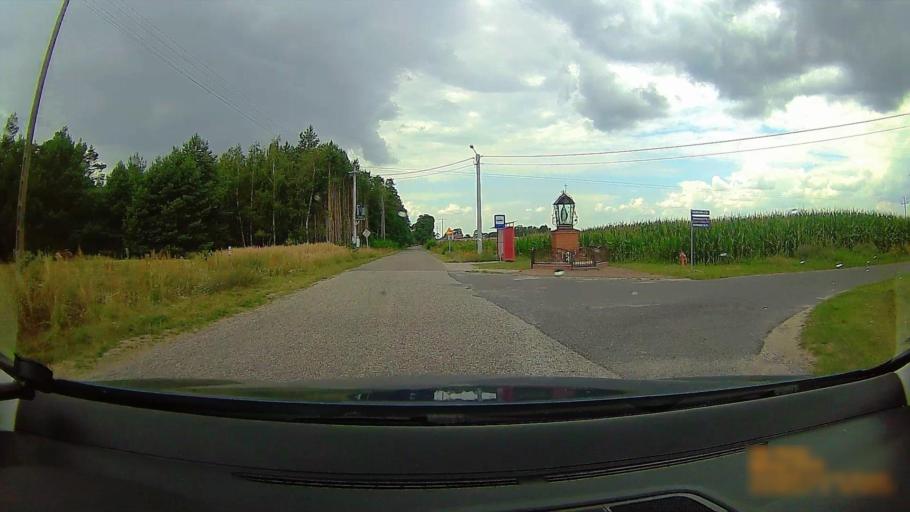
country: PL
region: Greater Poland Voivodeship
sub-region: Powiat koninski
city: Rychwal
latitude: 52.1040
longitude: 18.2049
